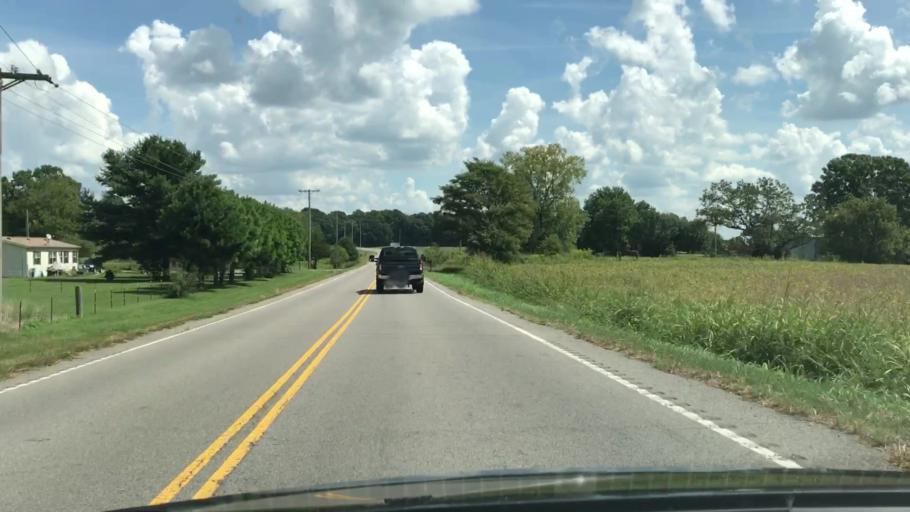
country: US
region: Tennessee
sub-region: Robertson County
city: Cross Plains
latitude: 36.5509
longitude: -86.7751
